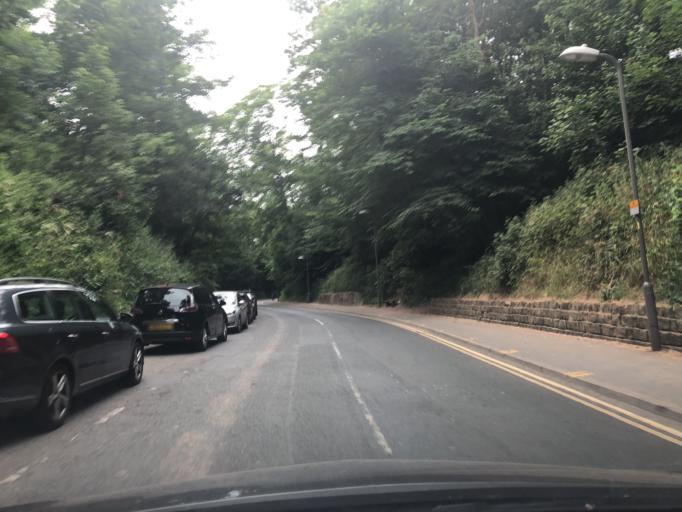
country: GB
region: England
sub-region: North Yorkshire
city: Filey
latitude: 54.2118
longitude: -0.2856
